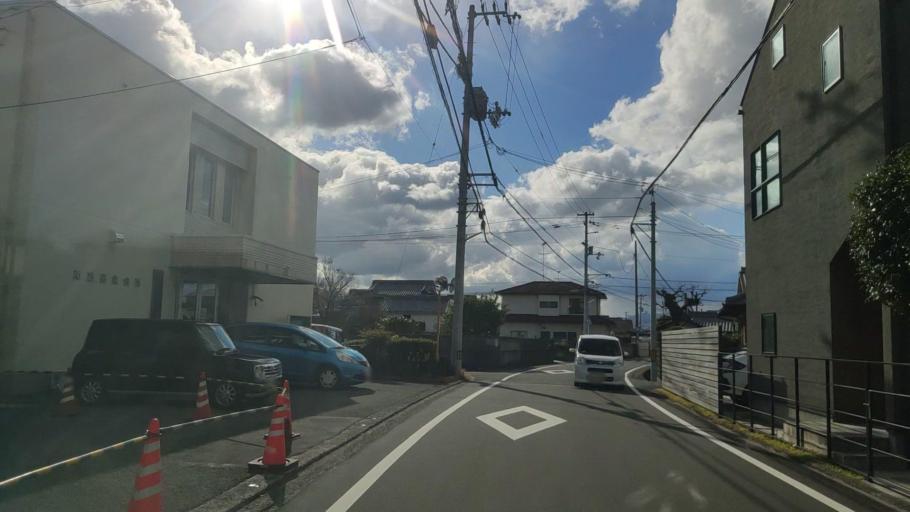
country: JP
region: Ehime
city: Masaki-cho
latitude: 33.8267
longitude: 132.7087
